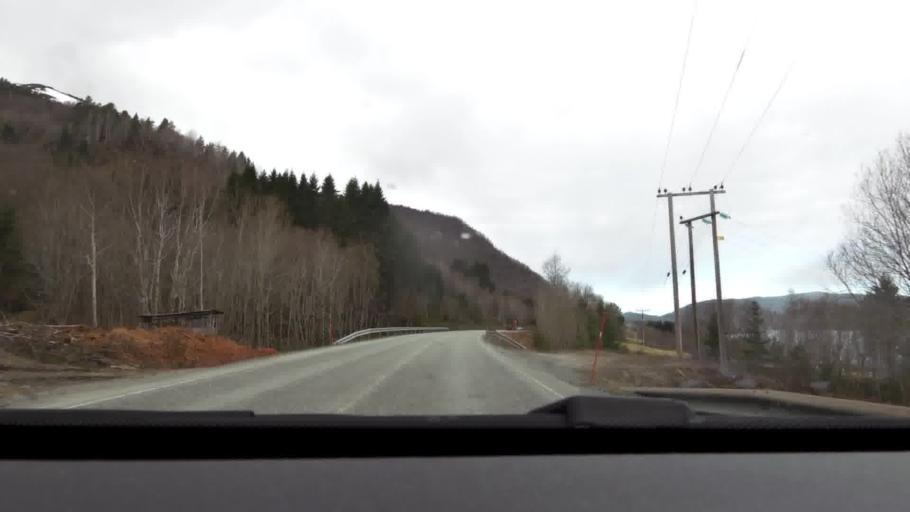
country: NO
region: More og Romsdal
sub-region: Eide
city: Eide
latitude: 62.9352
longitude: 7.4379
